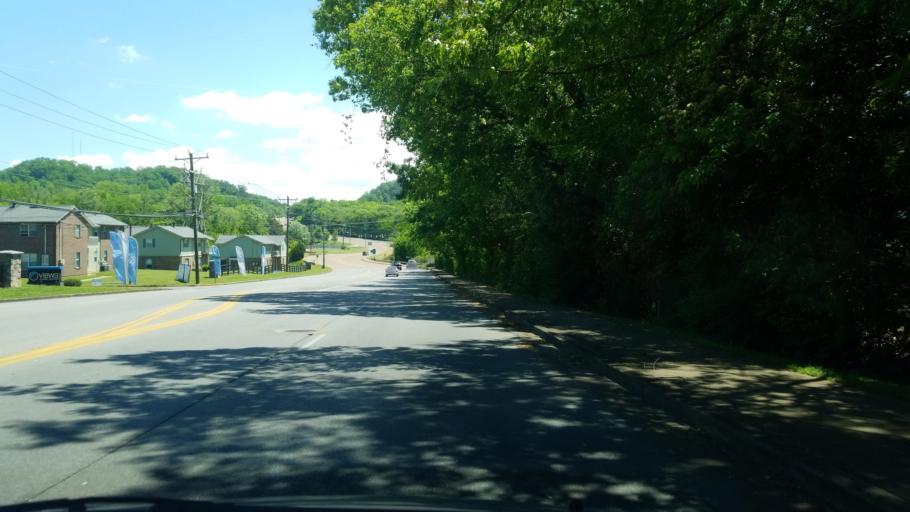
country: US
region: Tennessee
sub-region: Hamilton County
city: Red Bank
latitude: 35.1263
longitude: -85.3097
